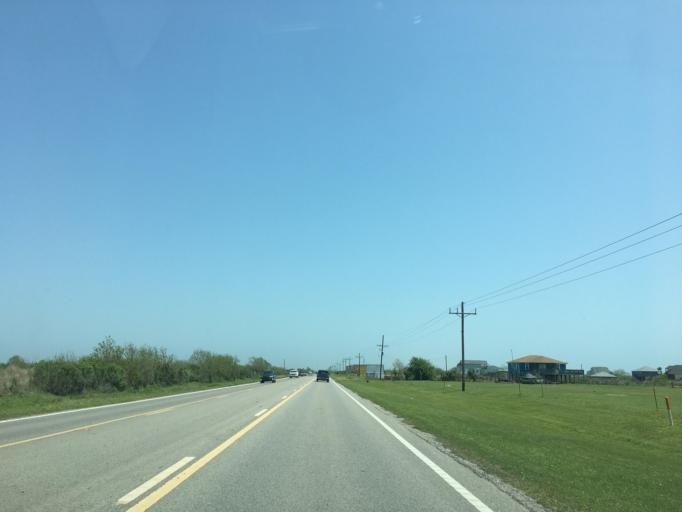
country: US
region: Texas
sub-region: Galveston County
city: Bolivar Peninsula
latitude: 29.4236
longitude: -94.6981
